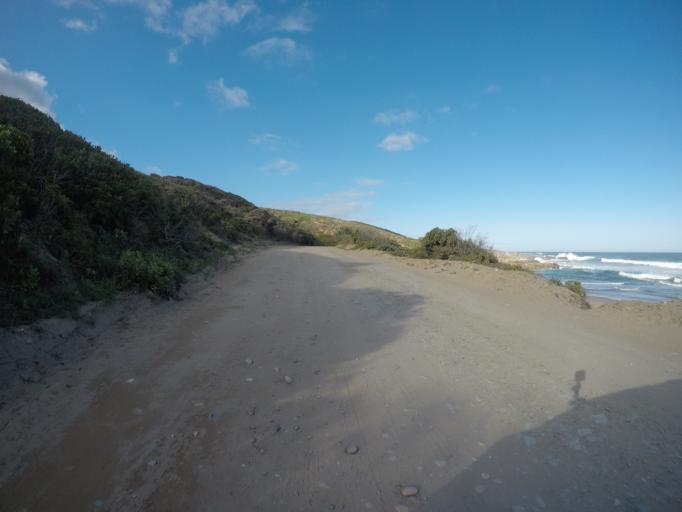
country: ZA
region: Western Cape
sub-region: Eden District Municipality
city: Riversdale
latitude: -34.4190
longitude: 21.3588
